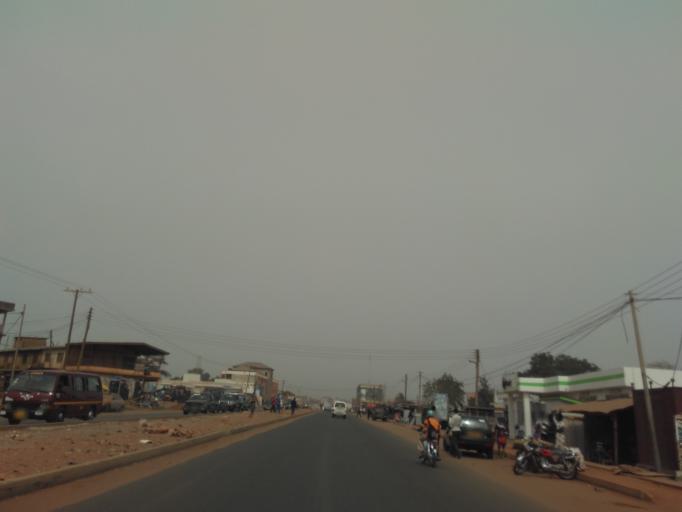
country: GH
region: Greater Accra
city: Tema
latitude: 5.6836
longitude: -0.0354
